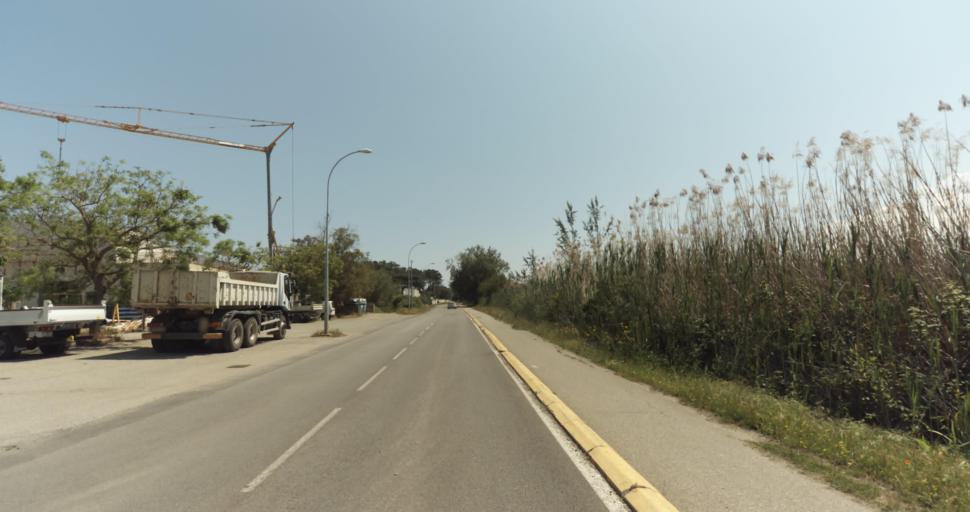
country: FR
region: Corsica
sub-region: Departement de la Haute-Corse
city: Biguglia
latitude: 42.6106
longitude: 9.4829
